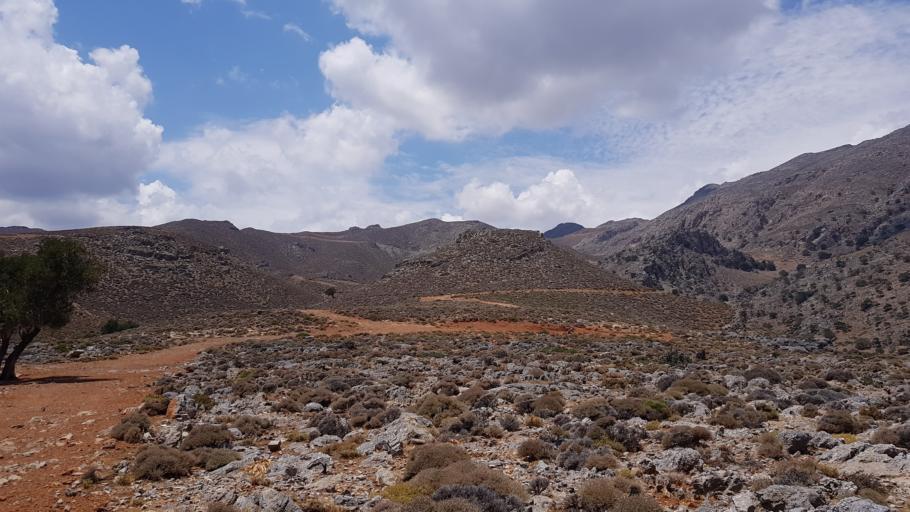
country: GR
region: Crete
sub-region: Nomos Irakleiou
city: Asimion
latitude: 34.9337
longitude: 25.0164
